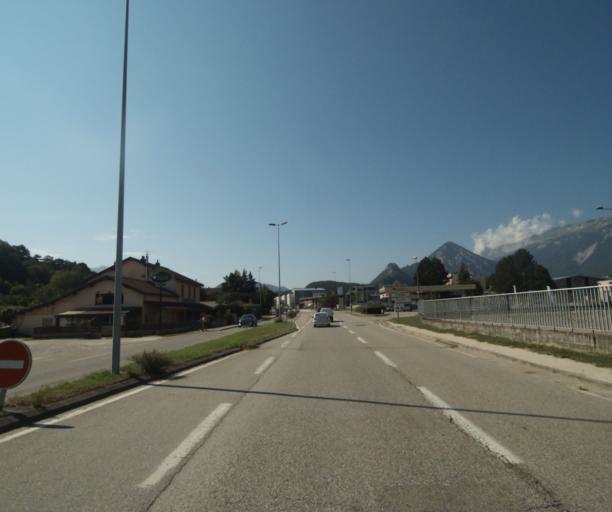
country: FR
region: Rhone-Alpes
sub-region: Departement de l'Isere
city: Allieres-et-Risset
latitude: 45.0982
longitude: 5.6841
